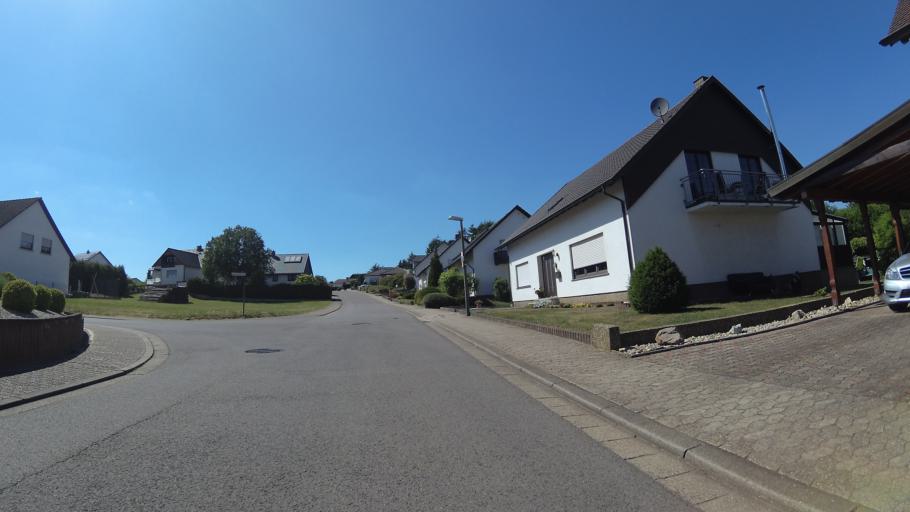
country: DE
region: Saarland
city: Saarwellingen
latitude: 49.3490
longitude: 6.8019
